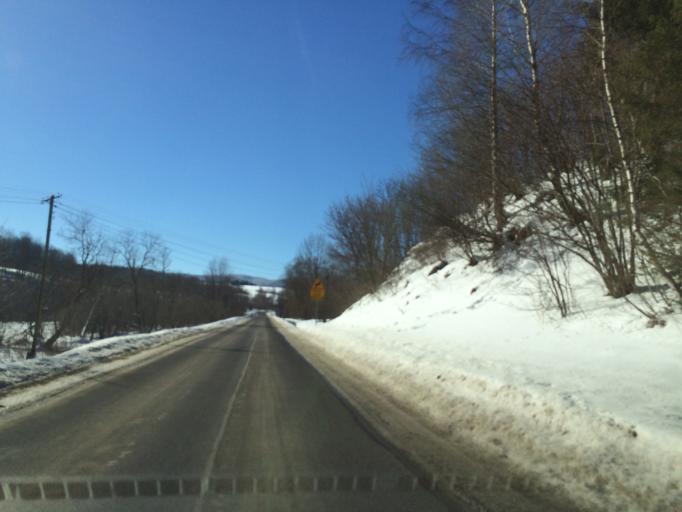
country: PL
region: Subcarpathian Voivodeship
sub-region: Powiat bieszczadzki
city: Lutowiska
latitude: 49.1147
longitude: 22.6627
